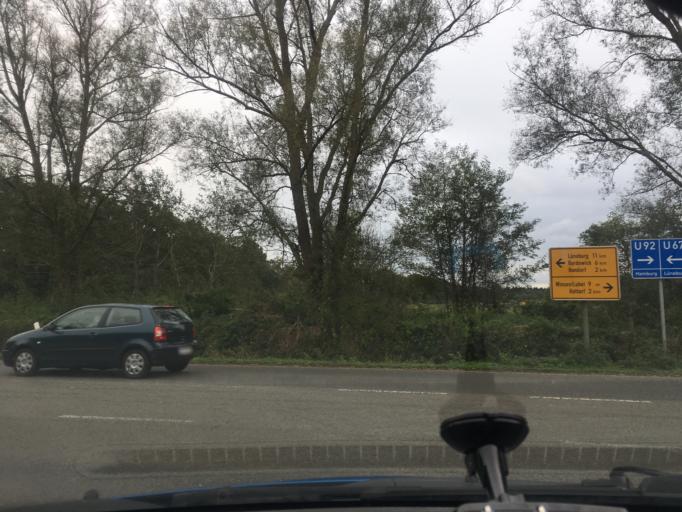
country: DE
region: Lower Saxony
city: Handorf
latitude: 53.3358
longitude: 10.3362
